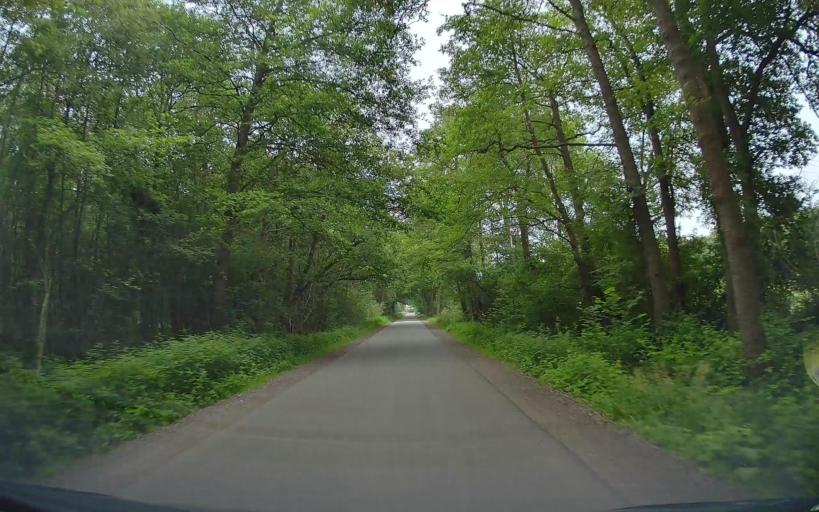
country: DE
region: Lower Saxony
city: Friesoythe
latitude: 53.0368
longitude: 7.8669
